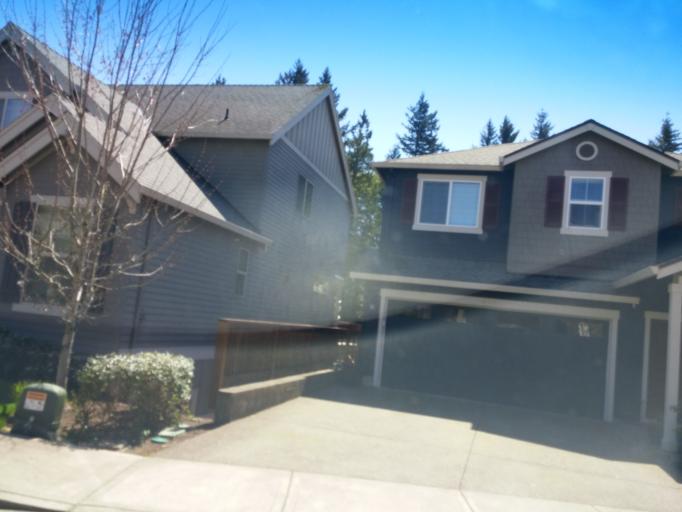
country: US
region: Oregon
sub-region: Washington County
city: West Haven
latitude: 45.5274
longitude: -122.7757
